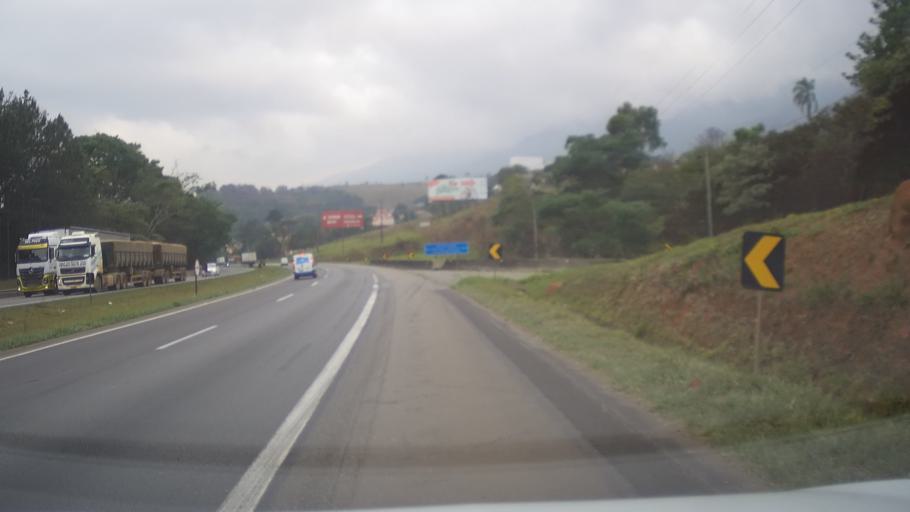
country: BR
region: Minas Gerais
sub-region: Extrema
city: Extrema
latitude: -22.8812
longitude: -46.3769
